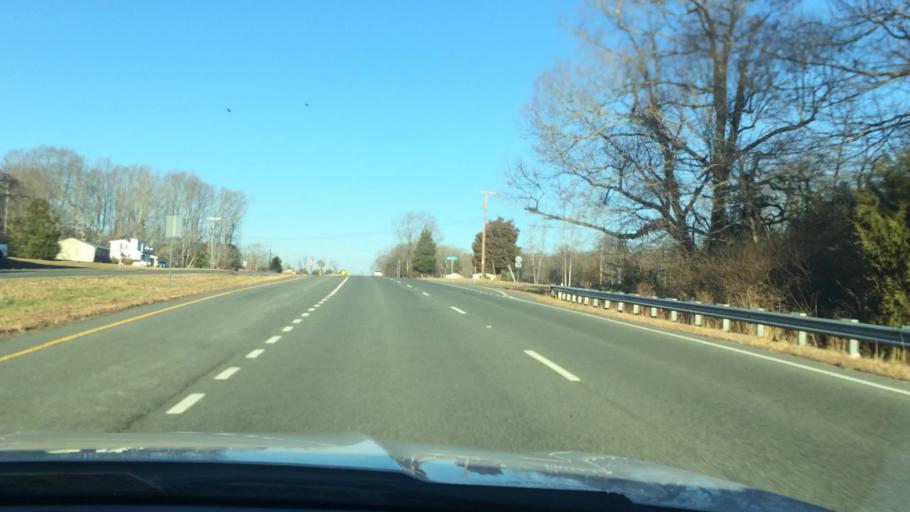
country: US
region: Virginia
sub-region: Lancaster County
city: Kilmarnock
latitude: 37.7460
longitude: -76.4010
